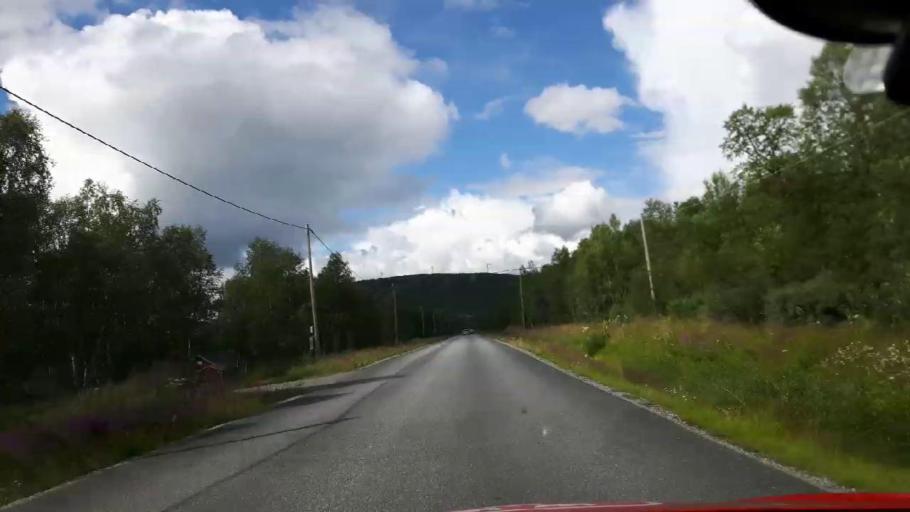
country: NO
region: Nordland
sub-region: Hattfjelldal
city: Hattfjelldal
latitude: 65.0643
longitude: 14.8407
